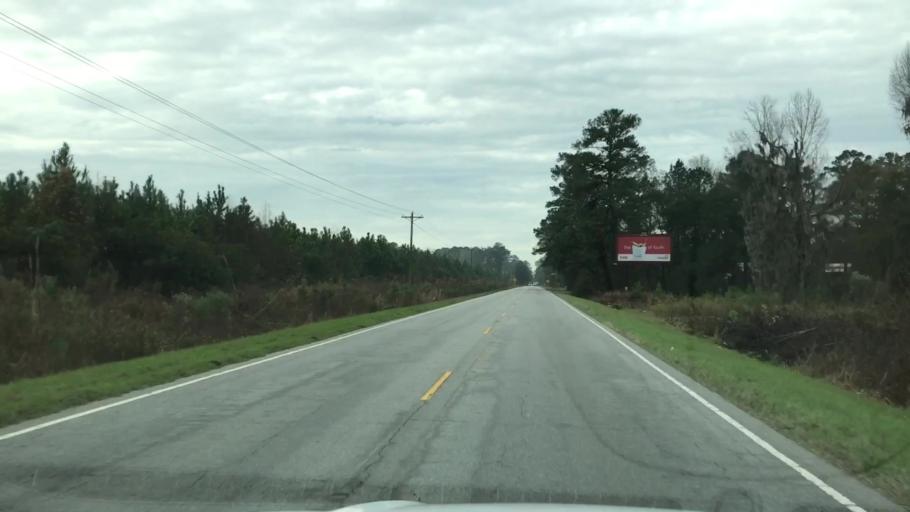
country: US
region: South Carolina
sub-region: Jasper County
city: Ridgeland
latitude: 32.4340
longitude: -80.8947
